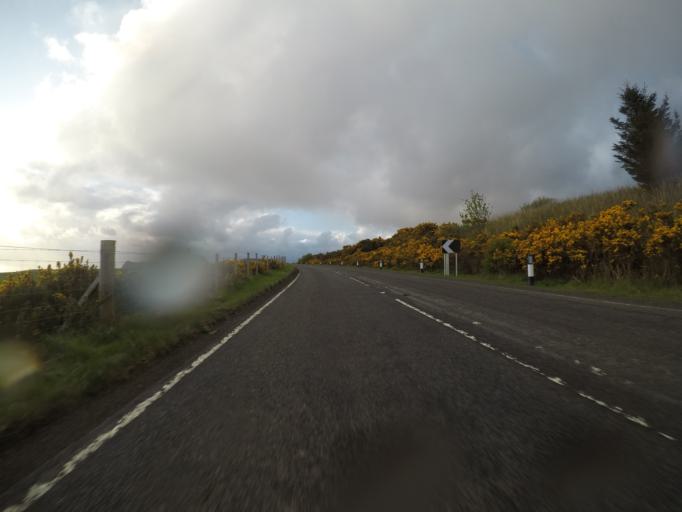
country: GB
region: Scotland
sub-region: Highland
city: Portree
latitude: 57.5721
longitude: -6.3641
